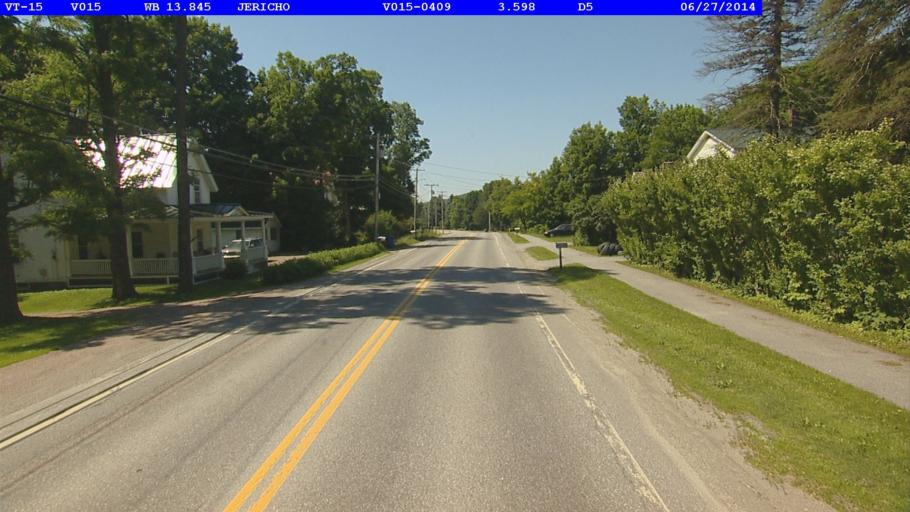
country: US
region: Vermont
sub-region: Chittenden County
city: Jericho
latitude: 44.5227
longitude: -72.9464
